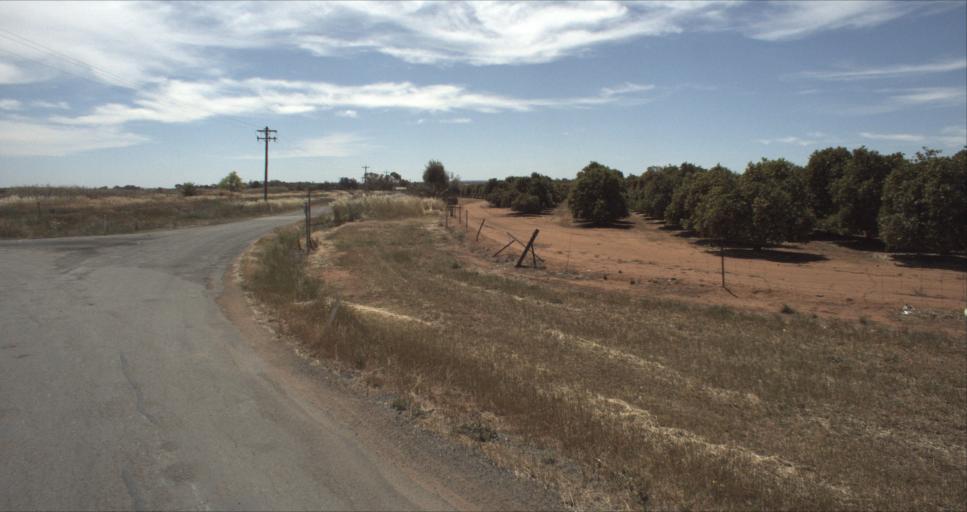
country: AU
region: New South Wales
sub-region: Leeton
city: Leeton
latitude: -34.6111
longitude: 146.4244
